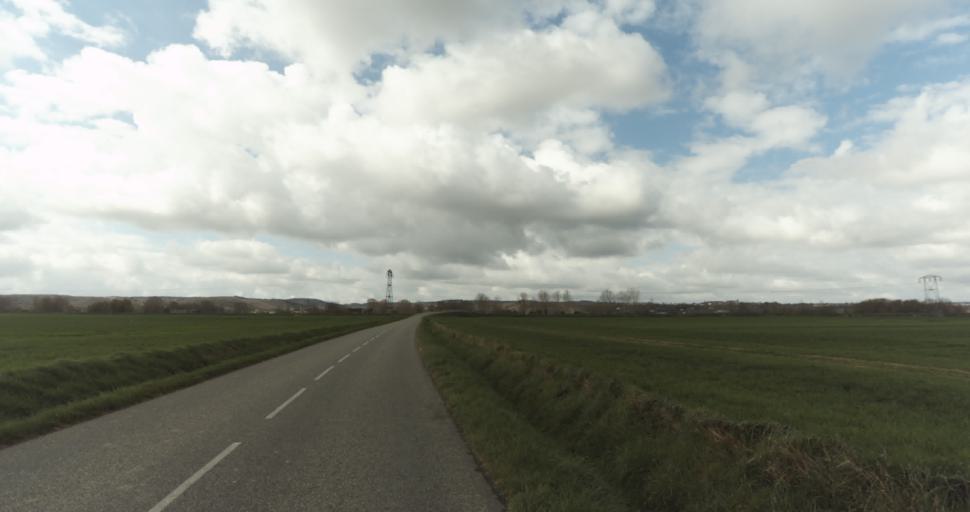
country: FR
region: Midi-Pyrenees
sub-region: Departement de la Haute-Garonne
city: Auterive
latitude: 43.3360
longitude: 1.4565
